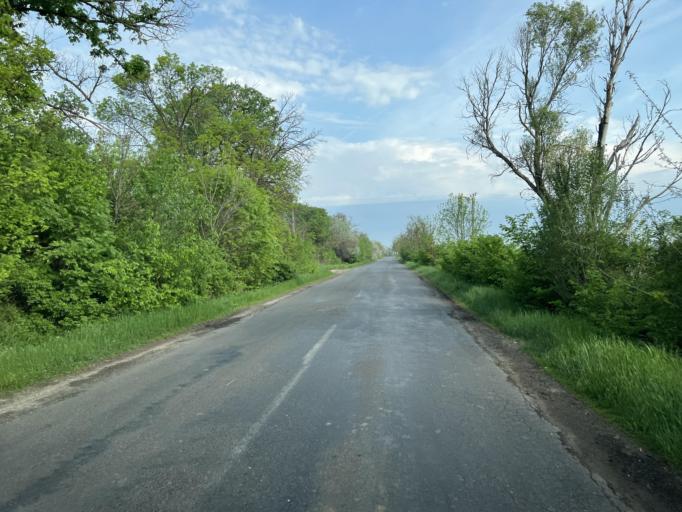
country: HU
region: Pest
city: Cegled
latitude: 47.2094
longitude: 19.7808
